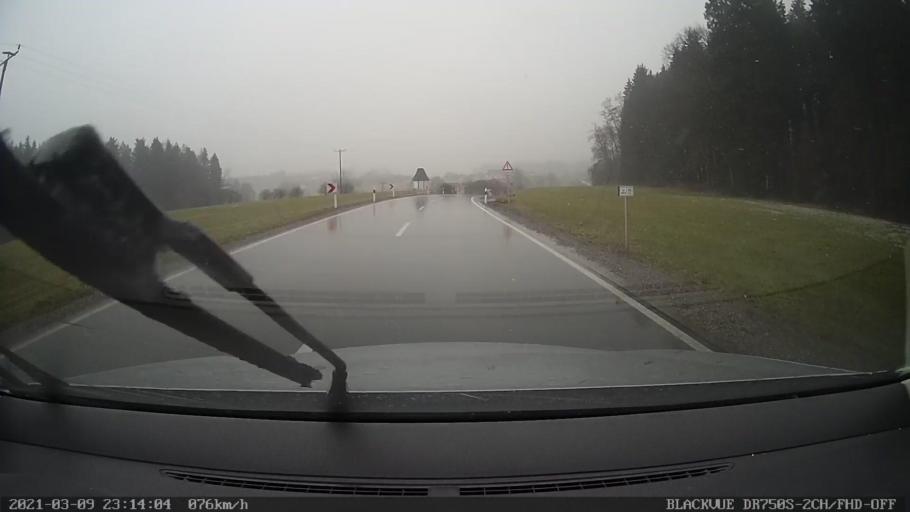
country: DE
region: Bavaria
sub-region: Upper Bavaria
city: Griesstatt
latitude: 47.9820
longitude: 12.2088
